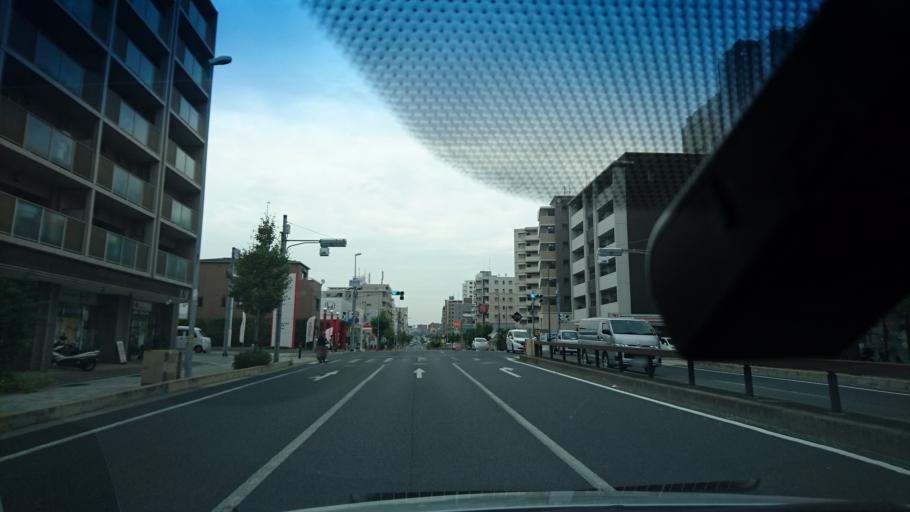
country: JP
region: Hyogo
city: Ashiya
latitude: 34.7274
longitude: 135.2894
